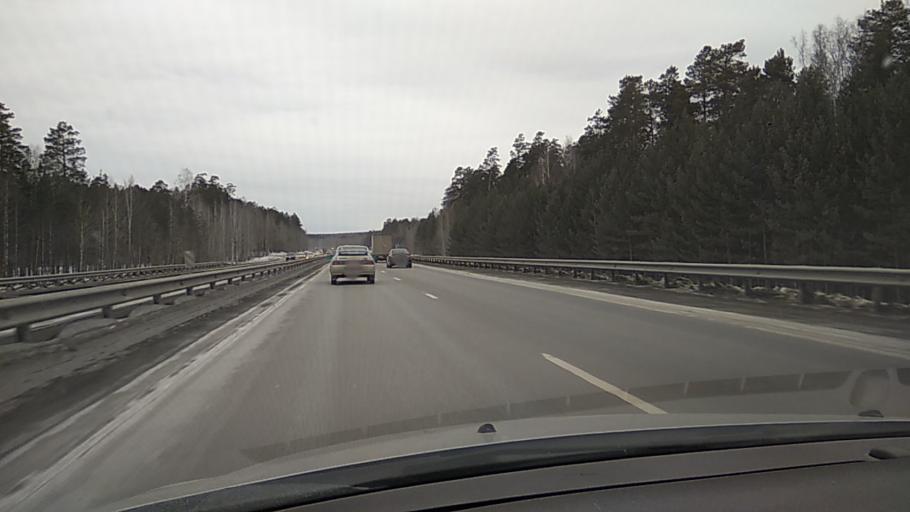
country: RU
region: Sverdlovsk
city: Talitsa
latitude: 56.8440
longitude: 60.0917
